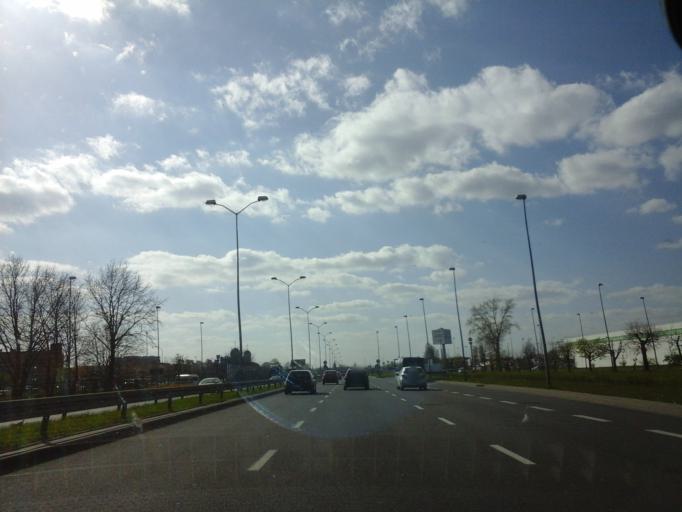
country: PL
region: West Pomeranian Voivodeship
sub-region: Szczecin
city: Szczecin
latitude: 53.3830
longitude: 14.6668
